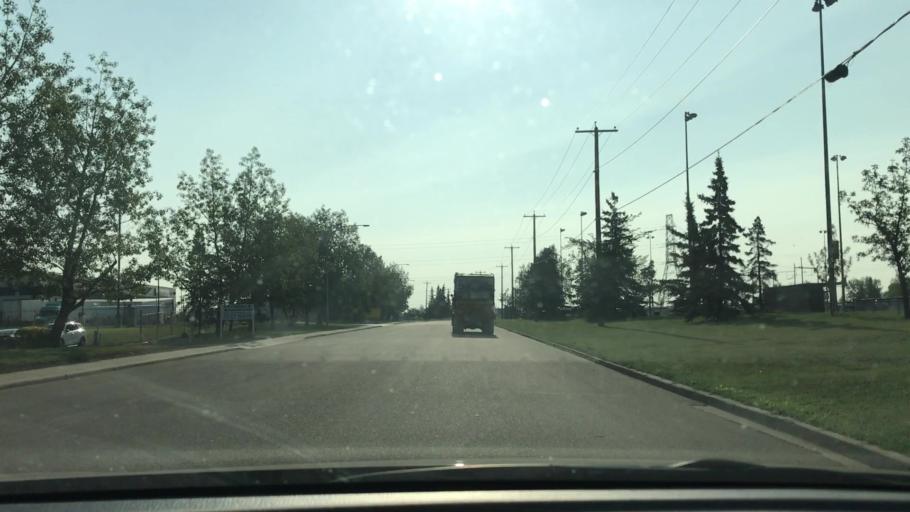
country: CA
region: Alberta
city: Edmonton
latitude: 53.4627
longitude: -113.4844
